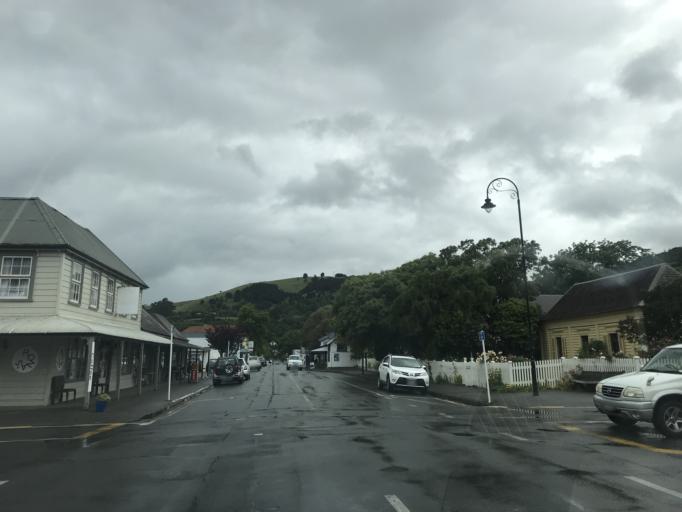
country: NZ
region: Canterbury
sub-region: Christchurch City
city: Christchurch
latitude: -43.8053
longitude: 172.9670
